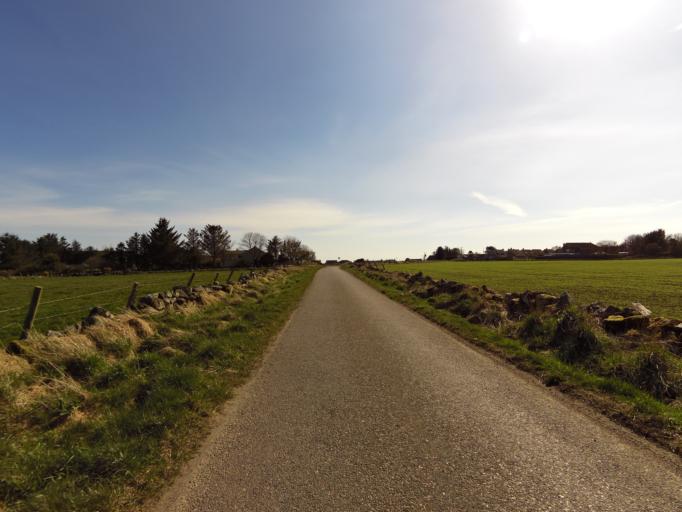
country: GB
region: Scotland
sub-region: Aberdeenshire
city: Portlethen
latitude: 57.0711
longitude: -2.1036
